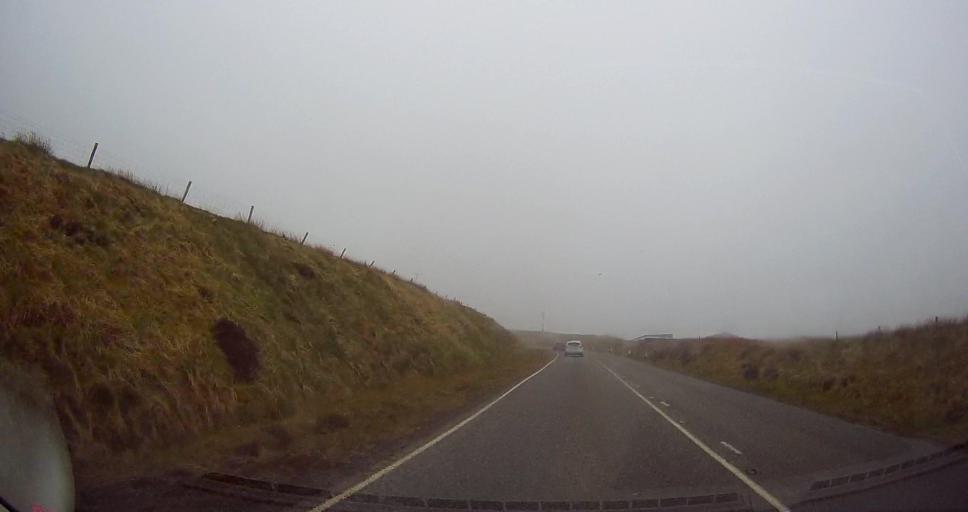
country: GB
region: Scotland
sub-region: Shetland Islands
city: Lerwick
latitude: 60.1386
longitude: -1.2337
